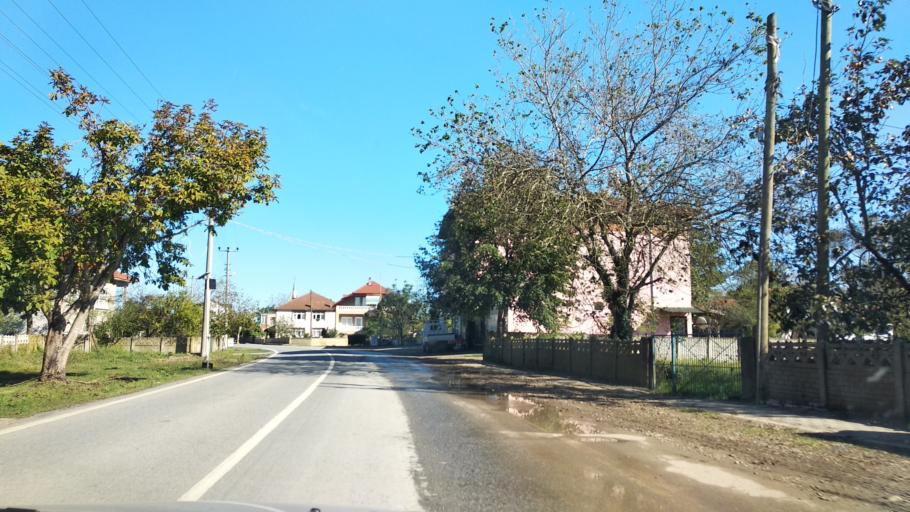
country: TR
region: Sakarya
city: Karasu
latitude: 41.1180
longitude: 30.6337
